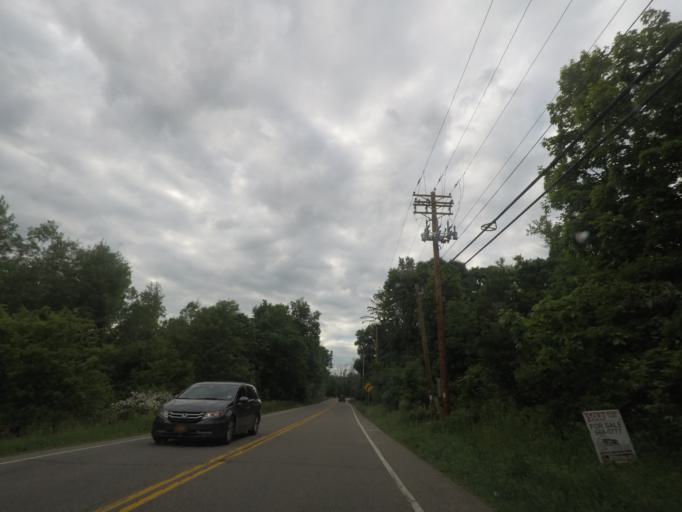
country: US
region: New York
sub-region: Orange County
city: Gardnertown
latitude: 41.5461
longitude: -74.0626
